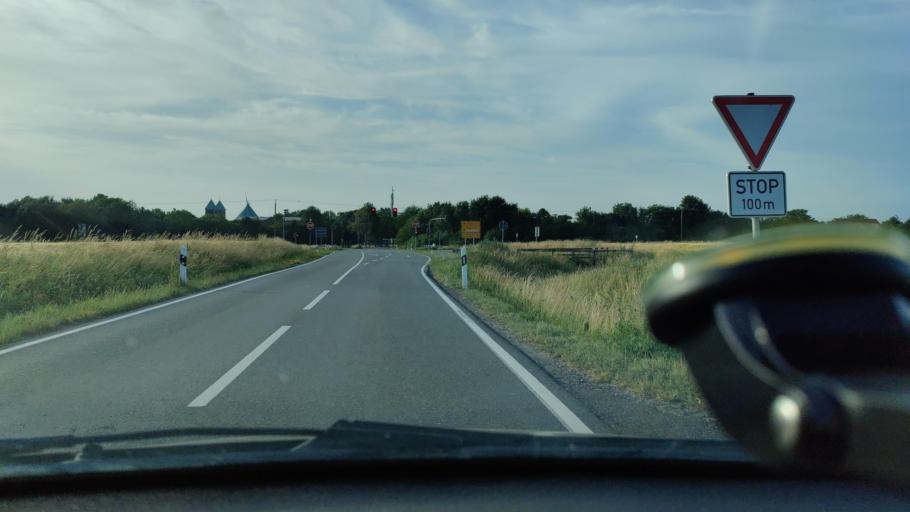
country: DE
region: North Rhine-Westphalia
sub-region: Regierungsbezirk Munster
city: Billerbeck
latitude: 52.0133
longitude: 7.2170
